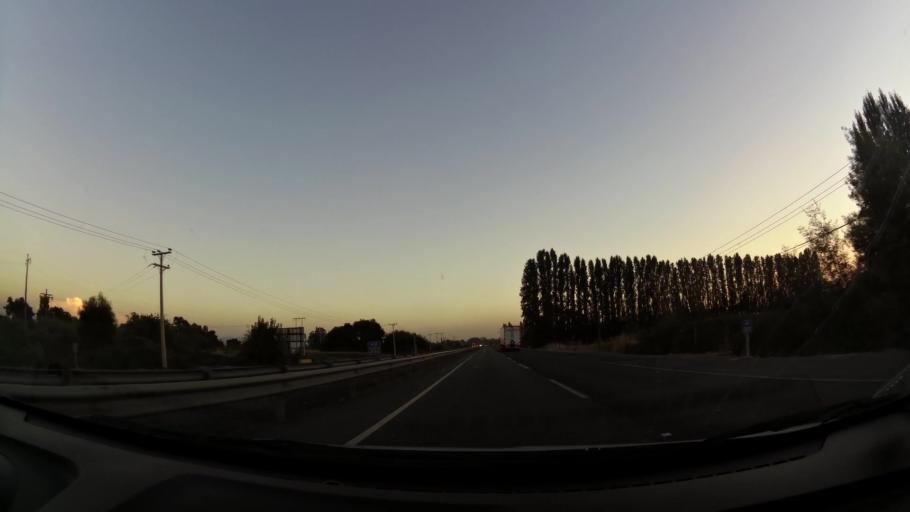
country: CL
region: Maule
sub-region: Provincia de Linares
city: Linares
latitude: -35.8488
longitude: -71.6294
